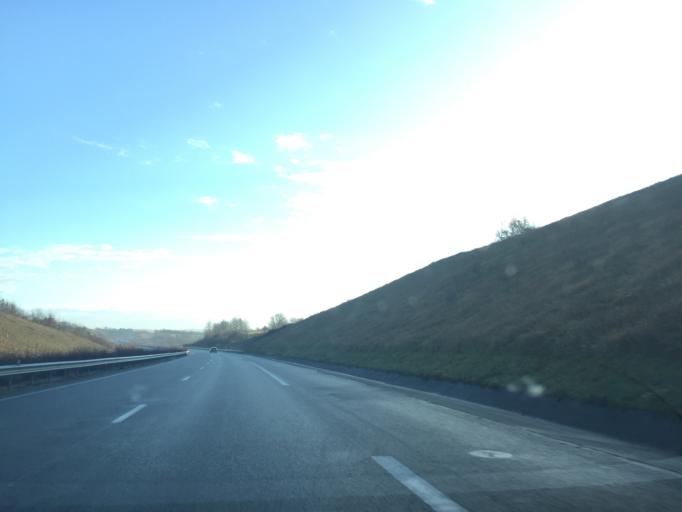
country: FR
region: Aquitaine
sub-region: Departement de la Dordogne
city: Thenon
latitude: 45.1532
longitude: 1.1022
